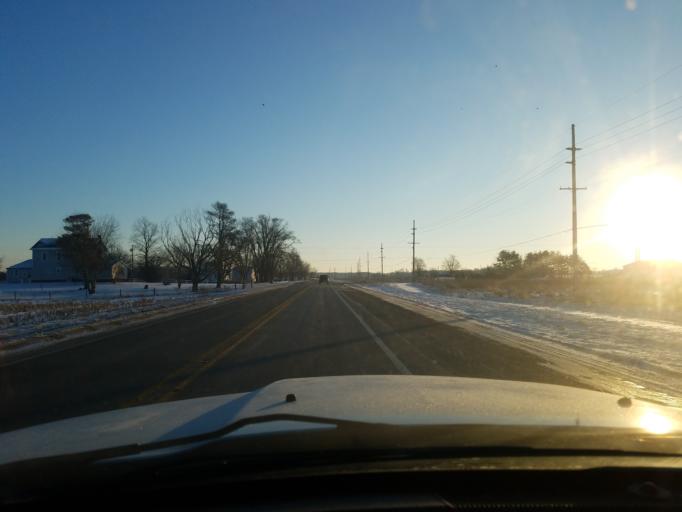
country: US
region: Indiana
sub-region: Marshall County
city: Bremen
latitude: 41.4538
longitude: -86.1193
